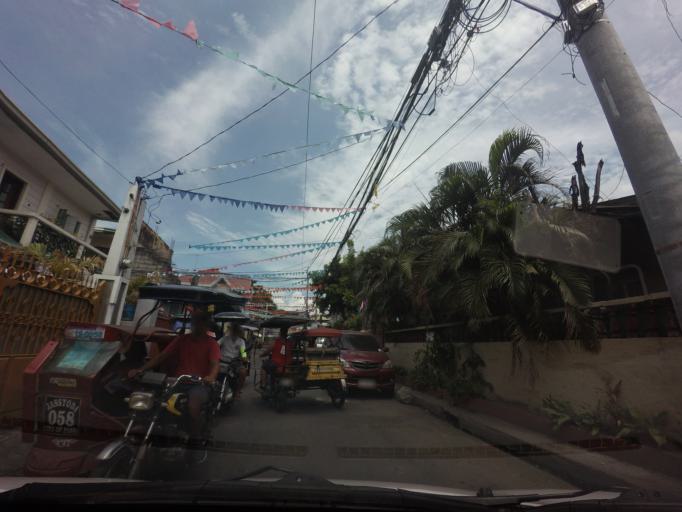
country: PH
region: Calabarzon
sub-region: Province of Rizal
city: Pateros
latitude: 14.5638
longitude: 121.0797
